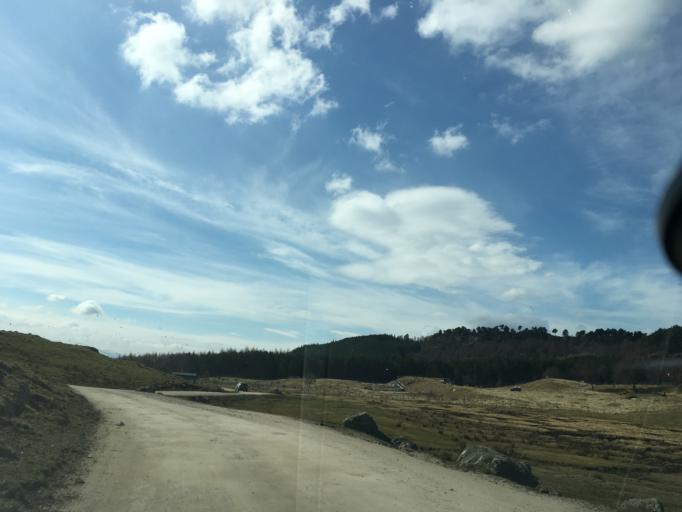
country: GB
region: Scotland
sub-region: Highland
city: Kingussie
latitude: 57.1107
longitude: -3.9781
